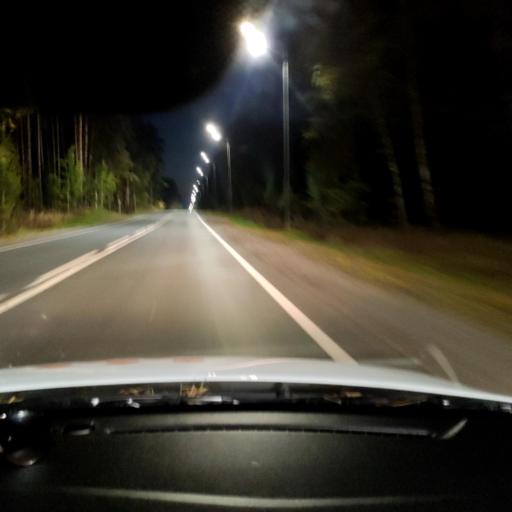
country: RU
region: Tatarstan
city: Verkhniy Uslon
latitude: 55.6386
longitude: 49.0399
